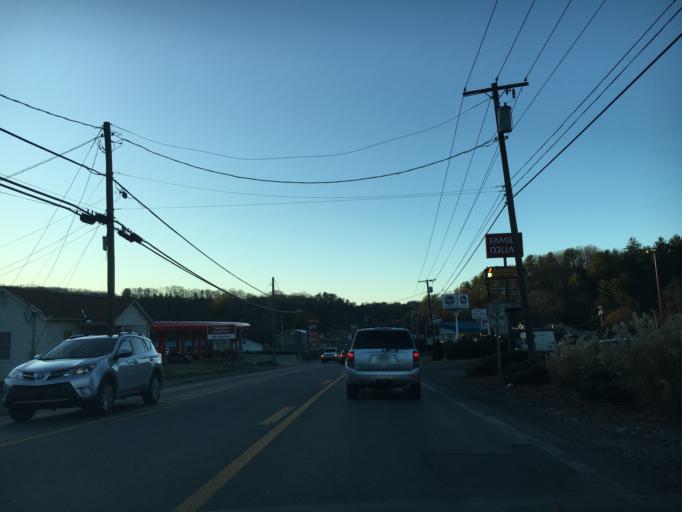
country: US
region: West Virginia
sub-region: Raleigh County
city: Beaver
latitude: 37.7492
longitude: -81.1363
